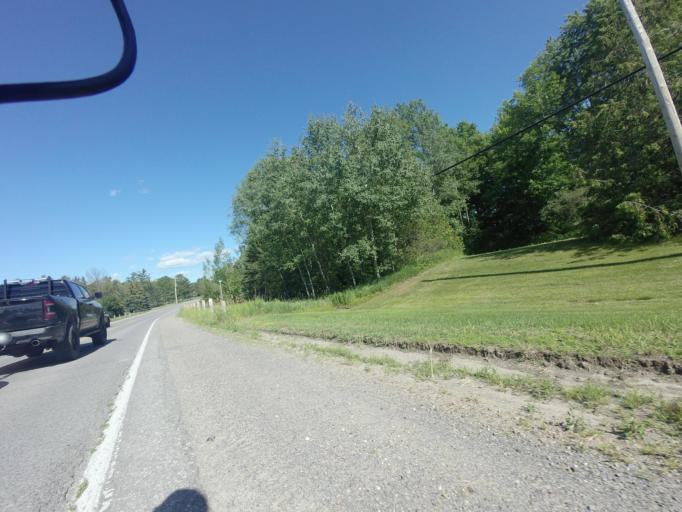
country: CA
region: Ontario
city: Arnprior
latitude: 45.4170
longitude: -76.4263
